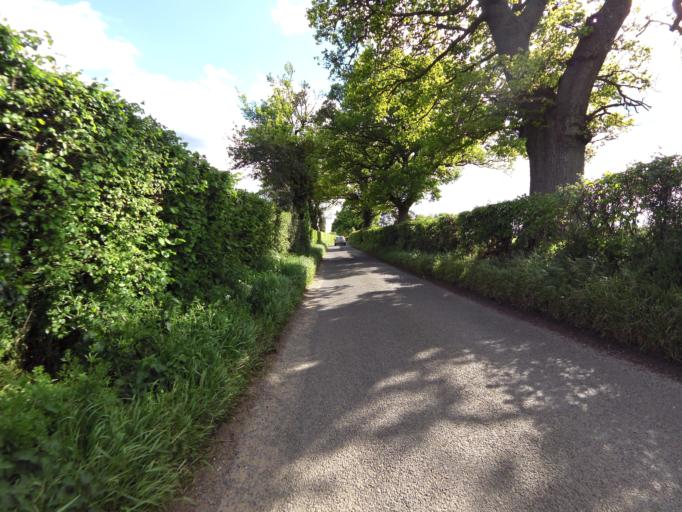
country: GB
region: England
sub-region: Suffolk
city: Woolpit
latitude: 52.2264
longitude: 0.8564
